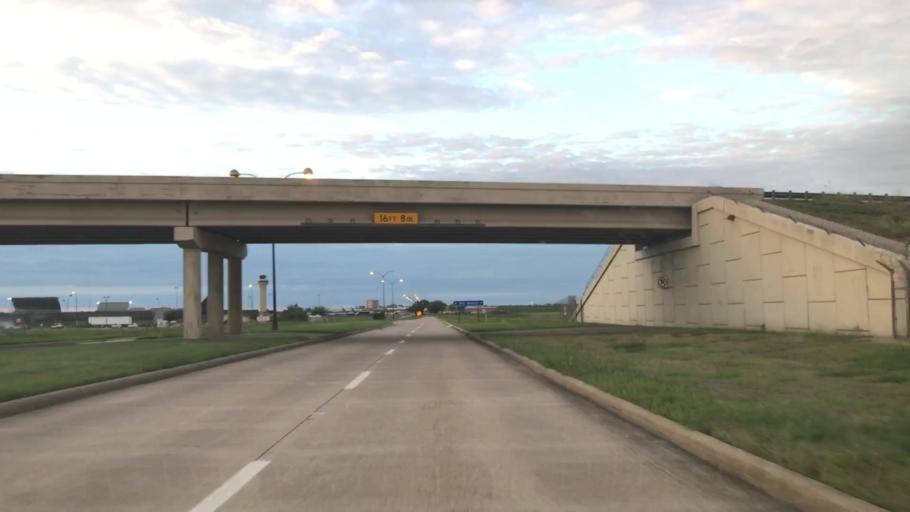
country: US
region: Texas
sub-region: Dallas County
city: Coppell
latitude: 32.8830
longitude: -97.0156
